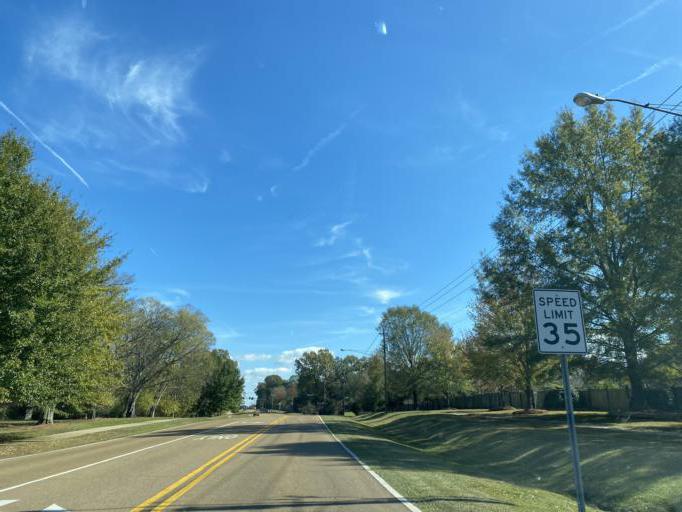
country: US
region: Mississippi
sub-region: Madison County
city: Madison
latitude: 32.4576
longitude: -90.1048
